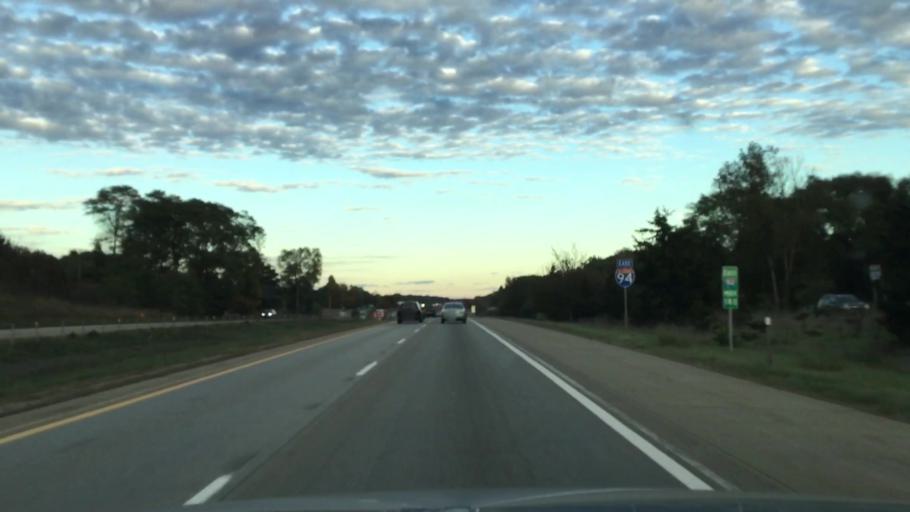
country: US
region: Michigan
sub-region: Jackson County
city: Grass Lake
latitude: 42.2918
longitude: -84.2455
